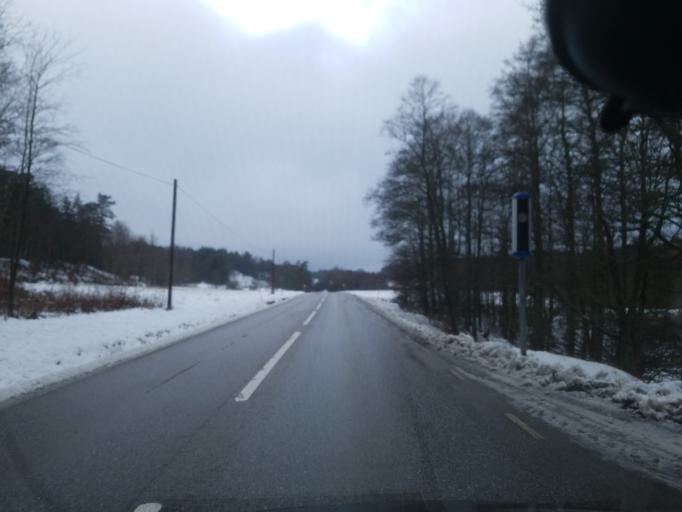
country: SE
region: Vaestra Goetaland
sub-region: Orust
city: Henan
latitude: 58.3056
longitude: 11.6077
